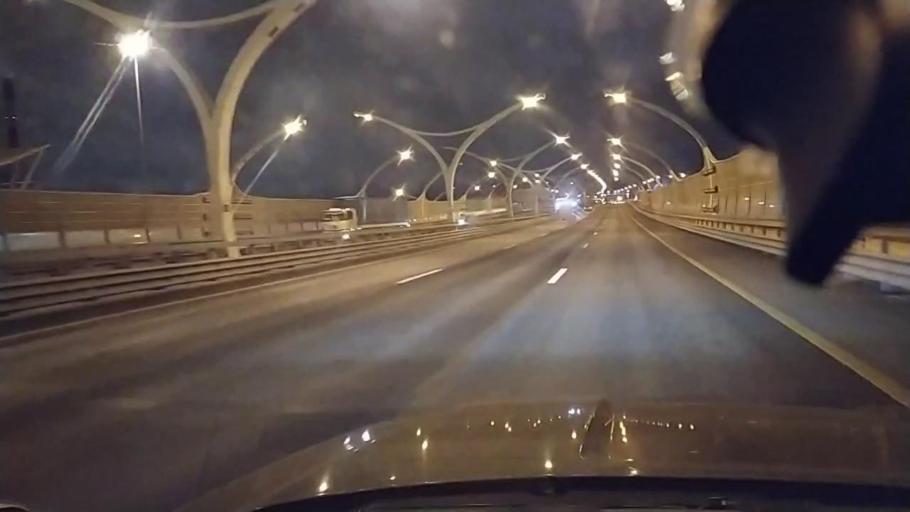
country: RU
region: St.-Petersburg
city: Staraya Derevnya
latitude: 60.0011
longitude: 30.2322
